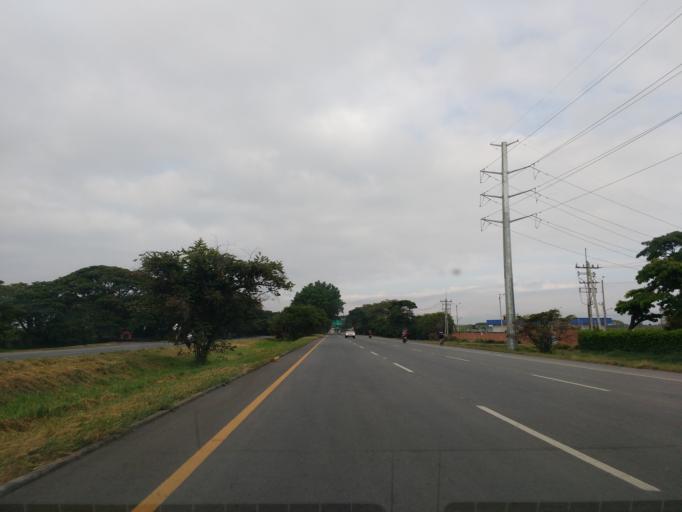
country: CO
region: Valle del Cauca
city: Yumbo
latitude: 3.5046
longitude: -76.4269
